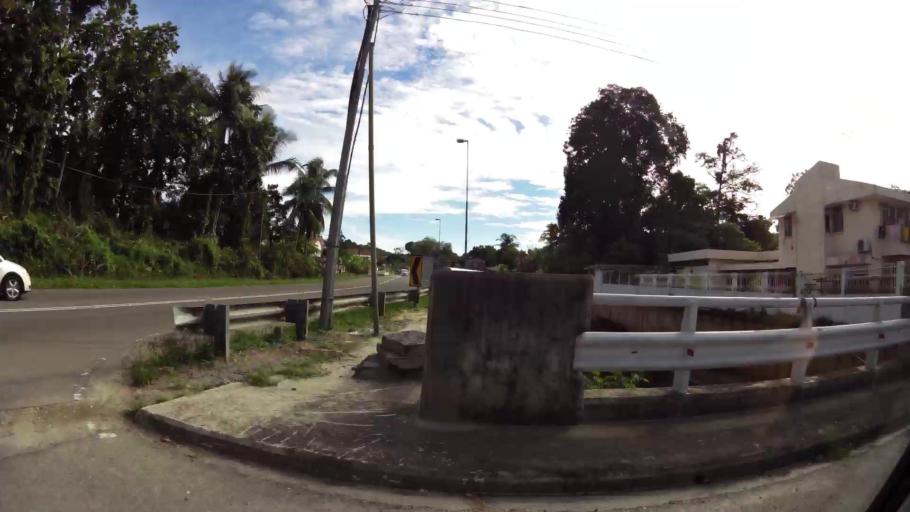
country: BN
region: Brunei and Muara
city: Bandar Seri Begawan
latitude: 4.8919
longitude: 114.9649
